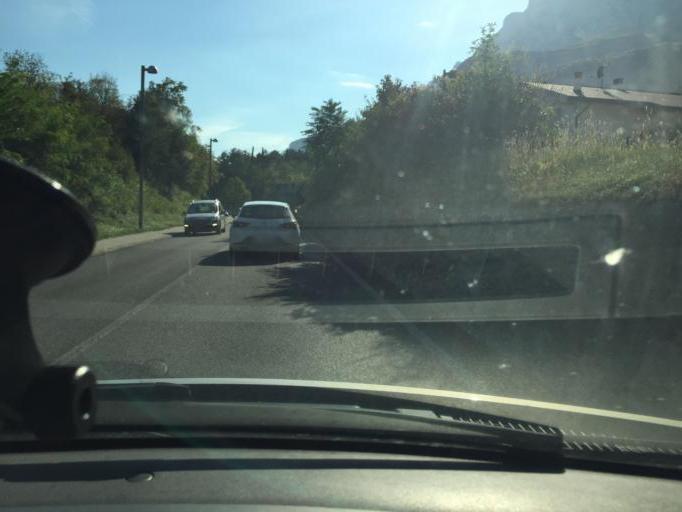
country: IT
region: Trentino-Alto Adige
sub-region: Provincia di Trento
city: Pietramurata
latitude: 46.0206
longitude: 10.9418
